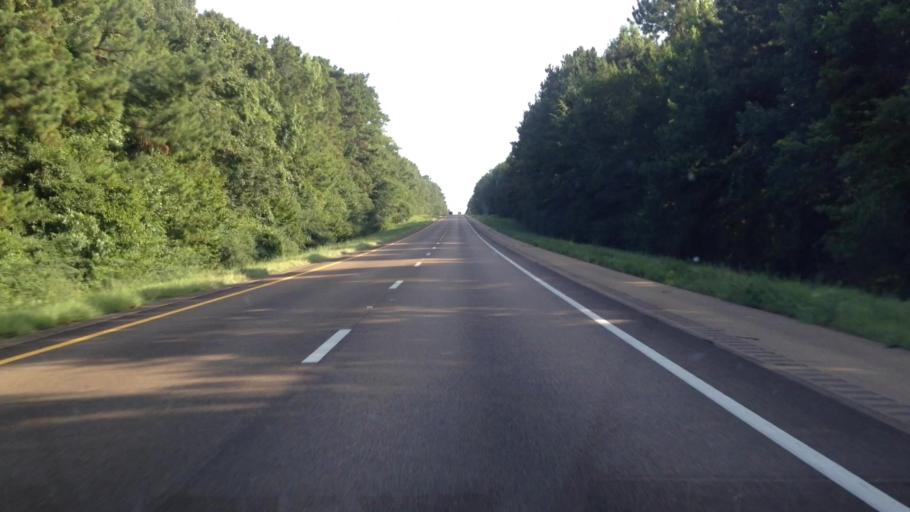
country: US
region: Mississippi
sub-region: Pike County
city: Summit
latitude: 31.3942
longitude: -90.4792
